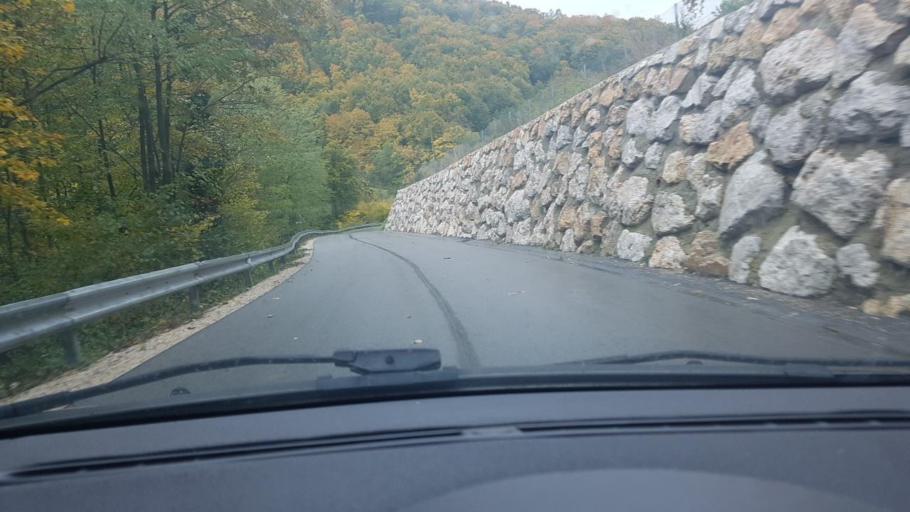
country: SI
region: Rogatec
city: Rogatec
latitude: 46.2653
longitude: 15.7053
